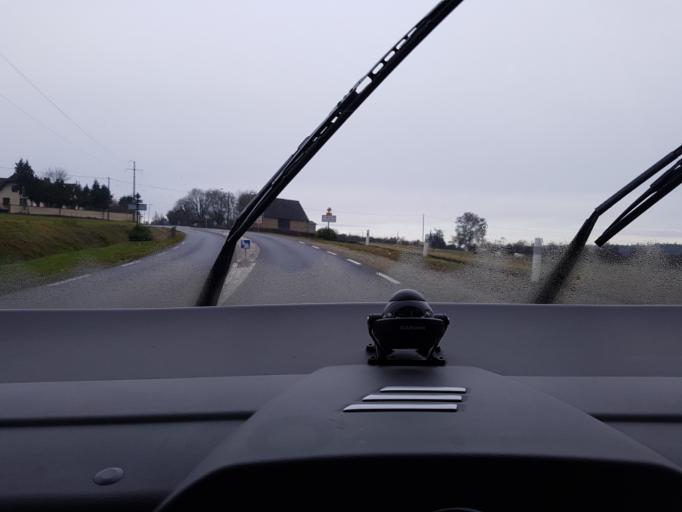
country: FR
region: Lower Normandy
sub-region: Departement de l'Orne
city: Saint-Sulpice-sur-Risle
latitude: 48.7888
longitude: 0.6724
